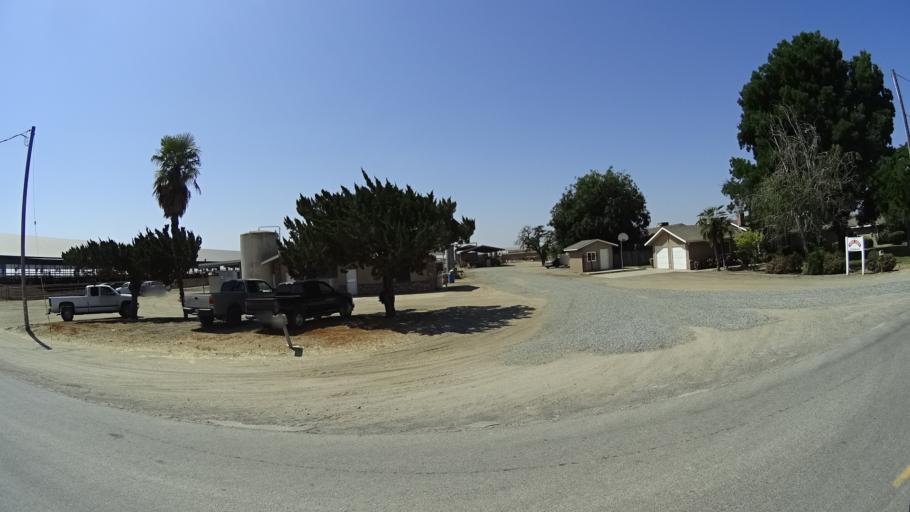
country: US
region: California
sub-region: Kings County
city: Hanford
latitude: 36.3717
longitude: -119.5951
